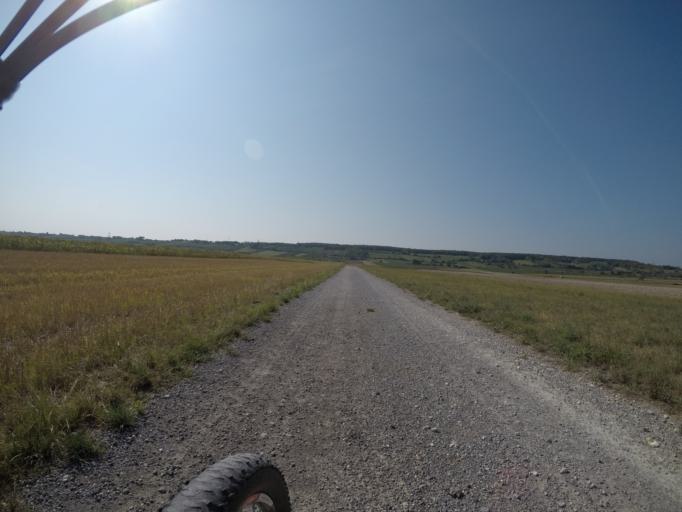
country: AT
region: Lower Austria
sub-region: Politischer Bezirk Baden
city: Hirtenberg
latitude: 47.9537
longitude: 16.1875
